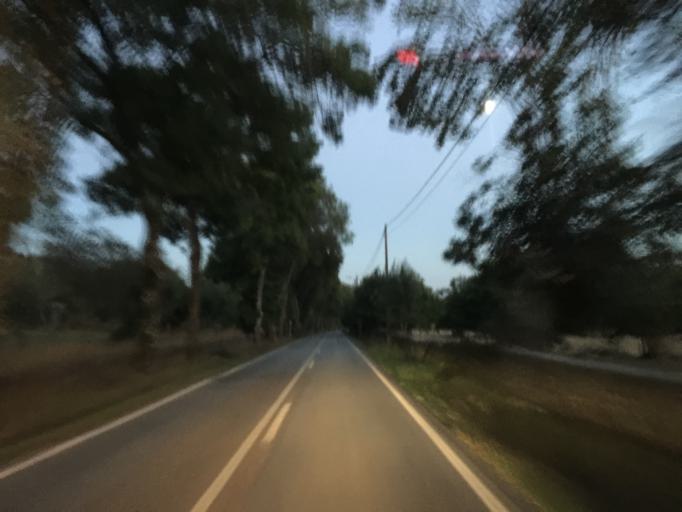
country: PT
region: Portalegre
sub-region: Marvao
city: Marvao
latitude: 39.3940
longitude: -7.4180
